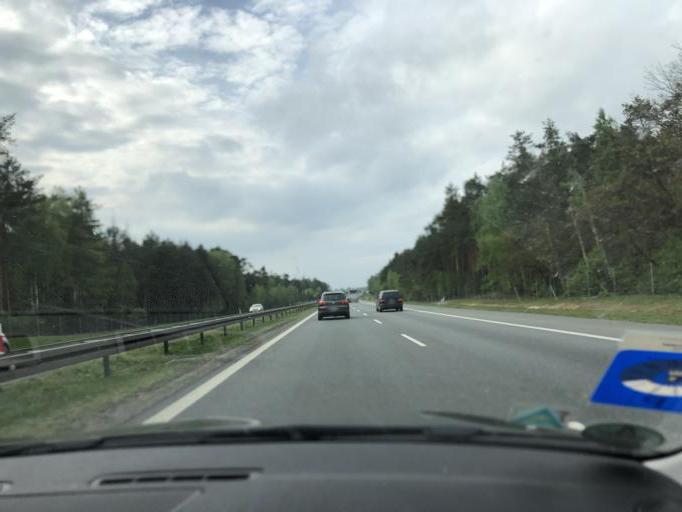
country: PL
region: Opole Voivodeship
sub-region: Powiat opolski
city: Dabrowa
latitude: 50.6331
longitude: 17.7430
